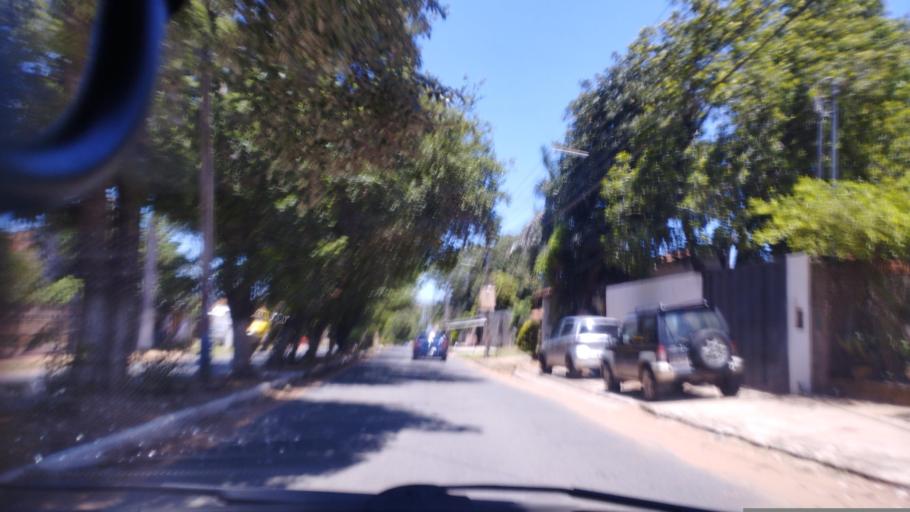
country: PY
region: Central
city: Nemby
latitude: -25.3772
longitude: -57.5419
